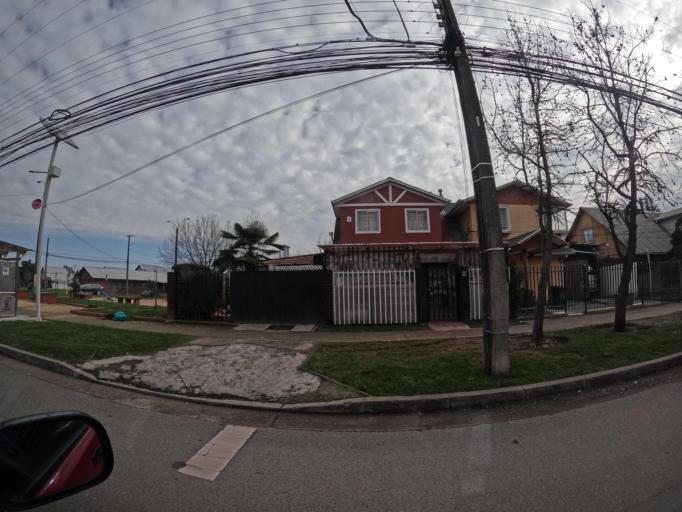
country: CL
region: Maule
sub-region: Provincia de Linares
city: Linares
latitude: -35.8345
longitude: -71.6014
